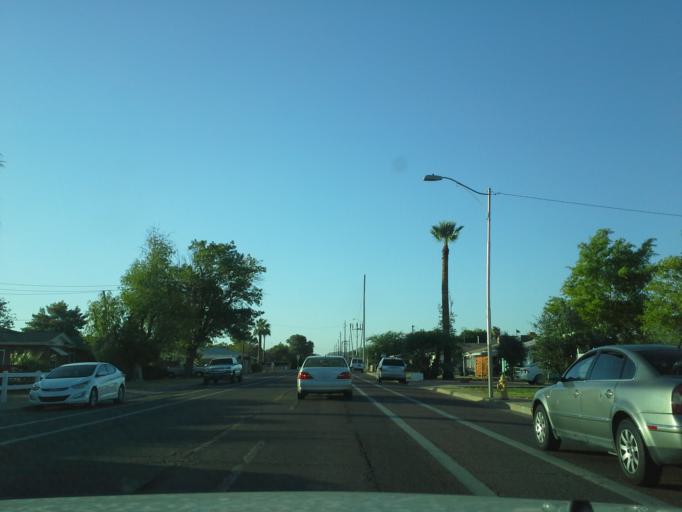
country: US
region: Arizona
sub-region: Maricopa County
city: Phoenix
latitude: 33.4972
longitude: -112.0781
